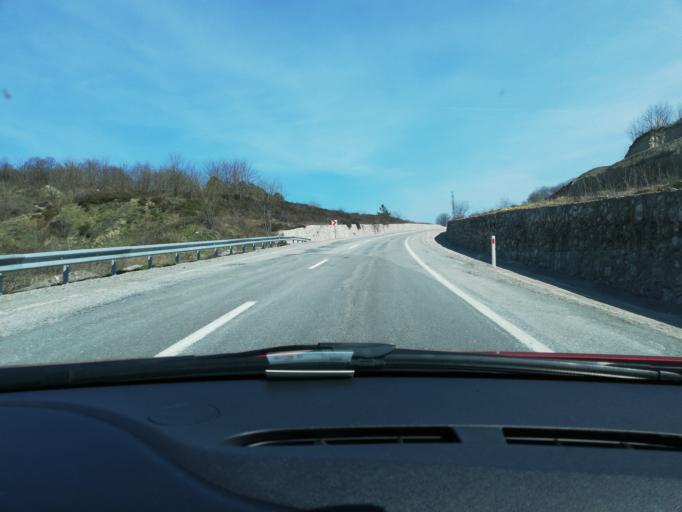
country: TR
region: Bartin
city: Amasra
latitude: 41.7284
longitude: 32.4067
